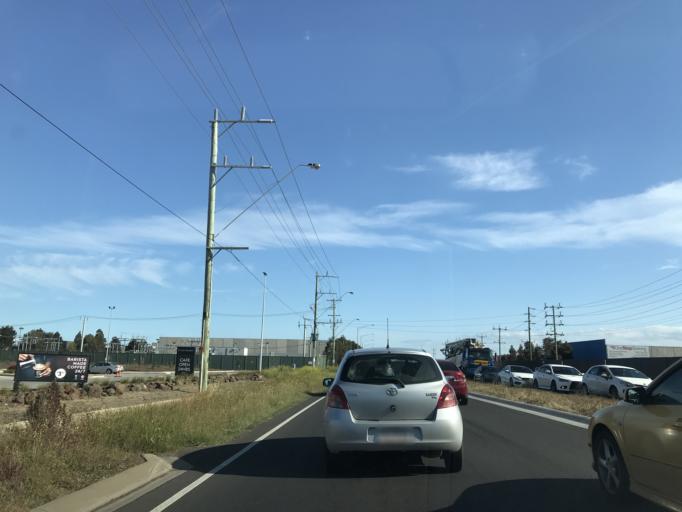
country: AU
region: Victoria
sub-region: Wyndham
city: Truganina
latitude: -37.8045
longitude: 144.7518
